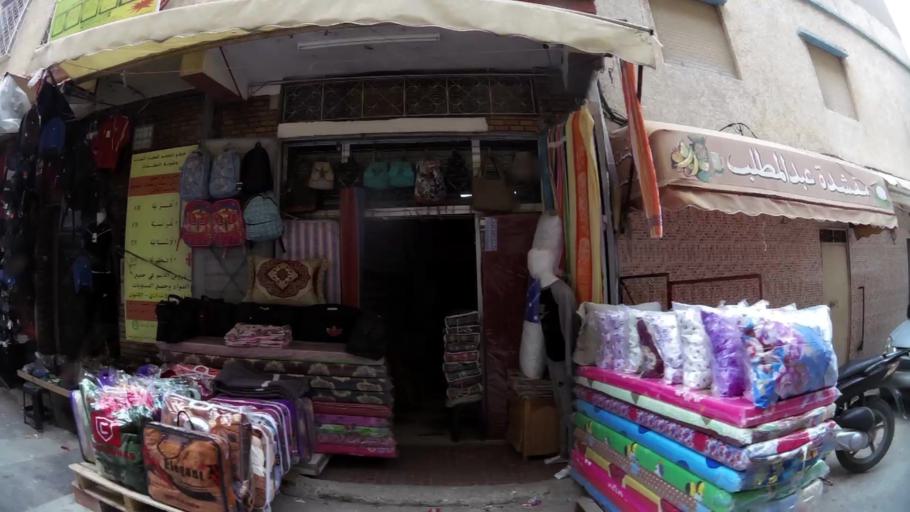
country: MA
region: Tanger-Tetouan
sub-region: Tanger-Assilah
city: Tangier
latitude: 35.7711
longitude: -5.7697
